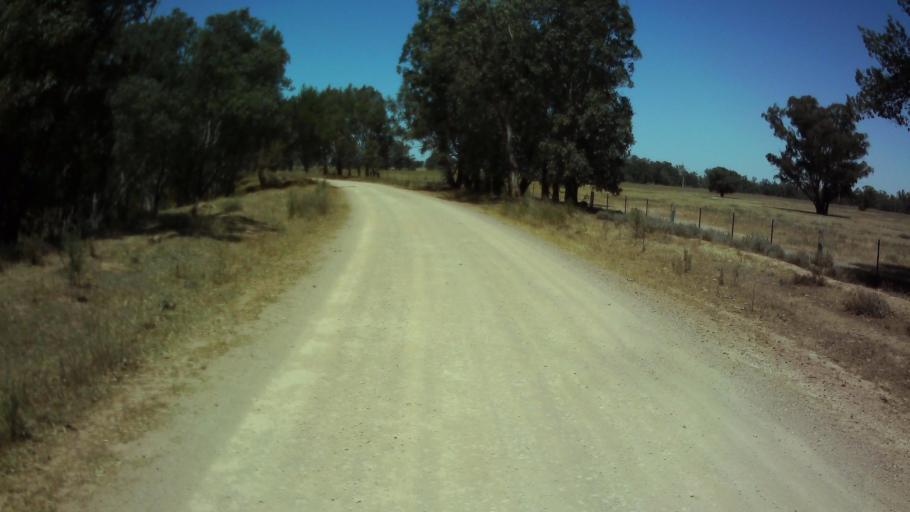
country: AU
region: New South Wales
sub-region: Weddin
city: Grenfell
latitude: -34.0290
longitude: 148.0150
